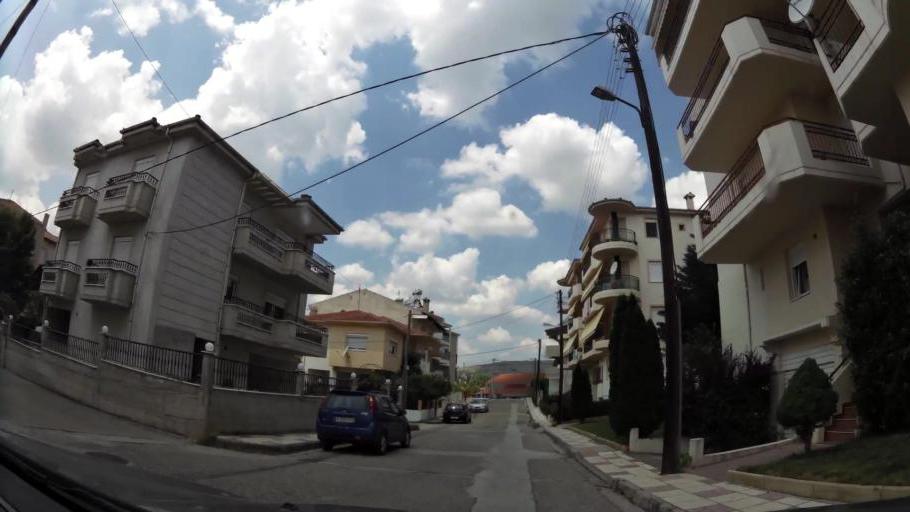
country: GR
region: West Macedonia
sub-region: Nomos Kozanis
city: Kozani
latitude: 40.2931
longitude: 21.7962
